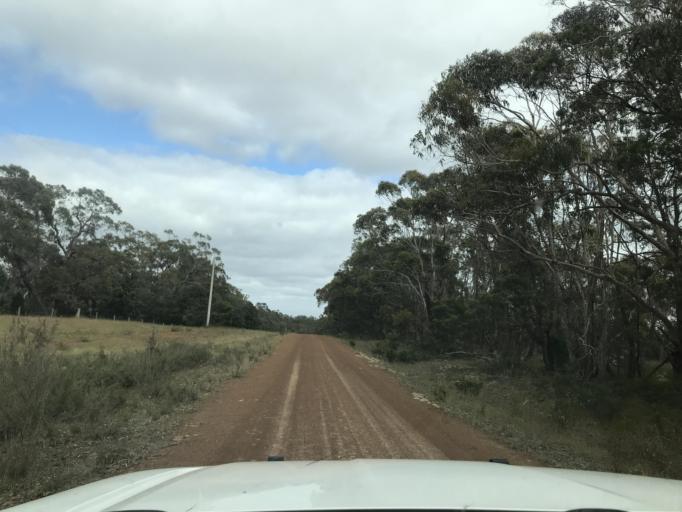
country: AU
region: South Australia
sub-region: Wattle Range
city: Penola
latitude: -37.3344
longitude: 141.4154
